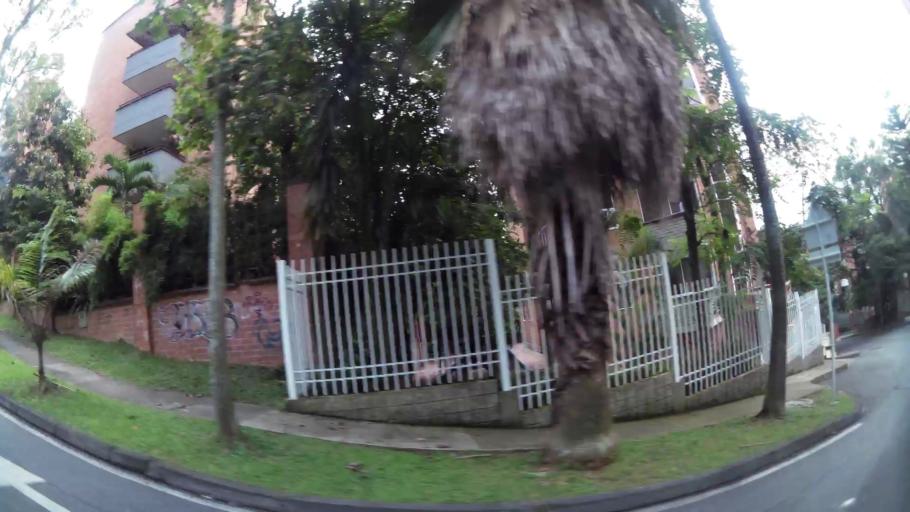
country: CO
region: Antioquia
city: Envigado
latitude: 6.1823
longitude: -75.5737
